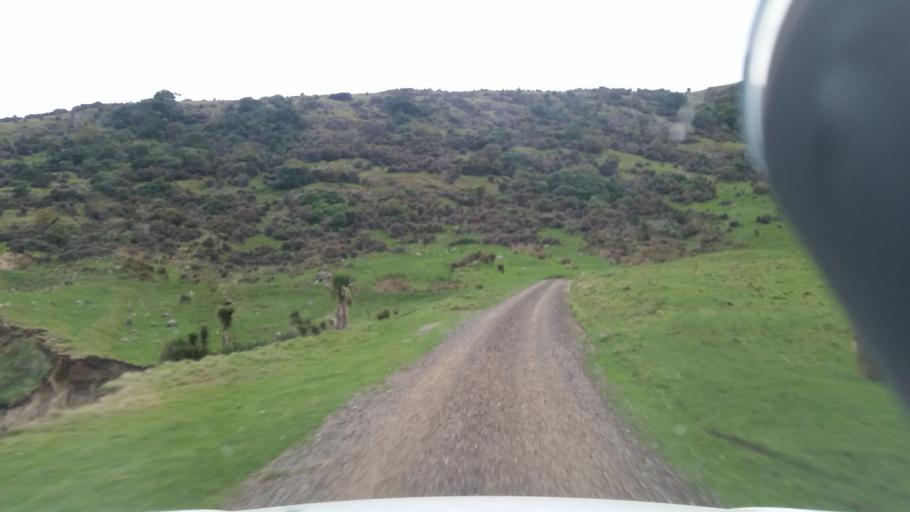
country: NZ
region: Canterbury
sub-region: Christchurch City
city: Christchurch
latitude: -43.8682
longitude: 173.0045
